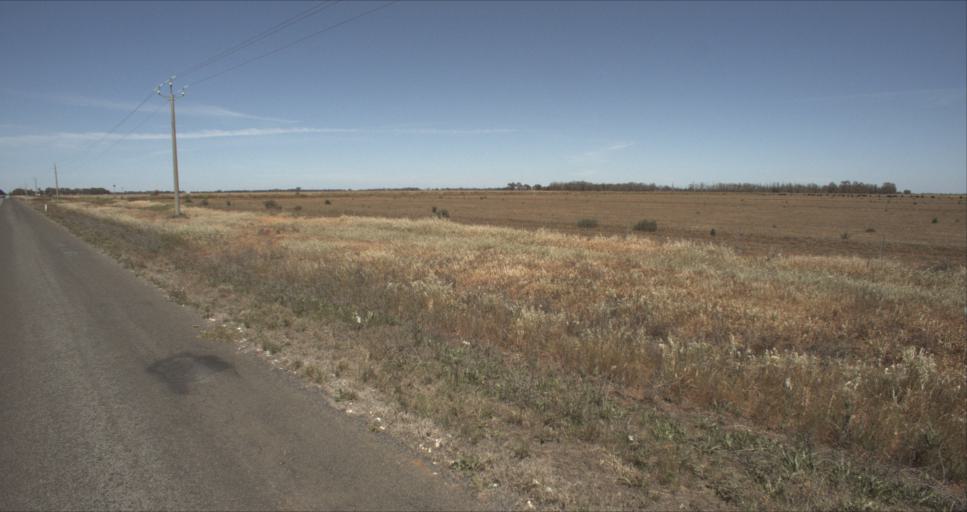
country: AU
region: New South Wales
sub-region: Leeton
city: Leeton
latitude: -34.4805
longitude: 146.2906
